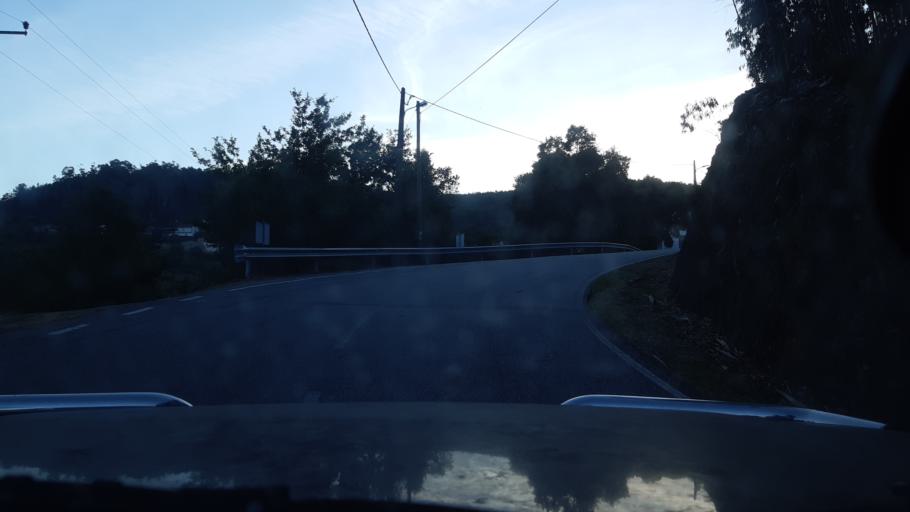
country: PT
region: Viseu
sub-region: Mortagua
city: Mortagua
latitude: 40.5433
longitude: -8.2745
